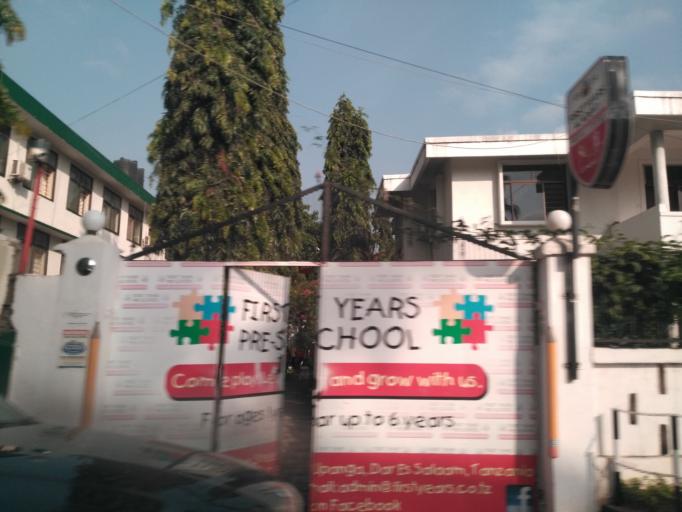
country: TZ
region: Dar es Salaam
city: Dar es Salaam
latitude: -6.8096
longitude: 39.2787
